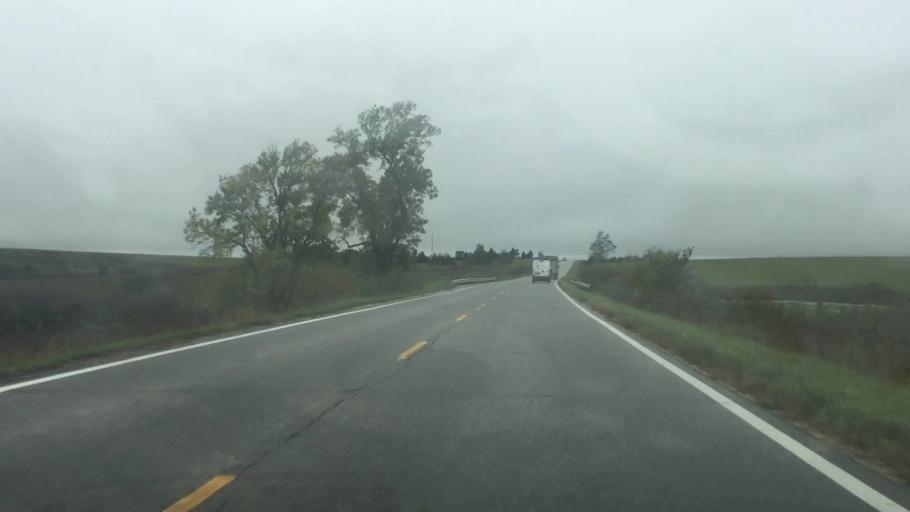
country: US
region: Kansas
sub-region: Anderson County
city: Garnett
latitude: 38.1792
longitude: -95.2671
